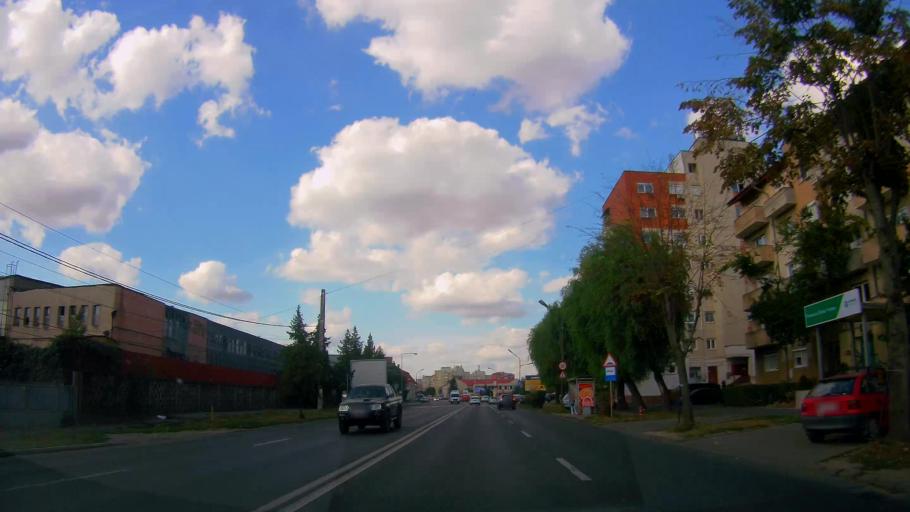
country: RO
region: Satu Mare
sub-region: Municipiul Satu Mare
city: Satu Mare
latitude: 47.7747
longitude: 22.8838
